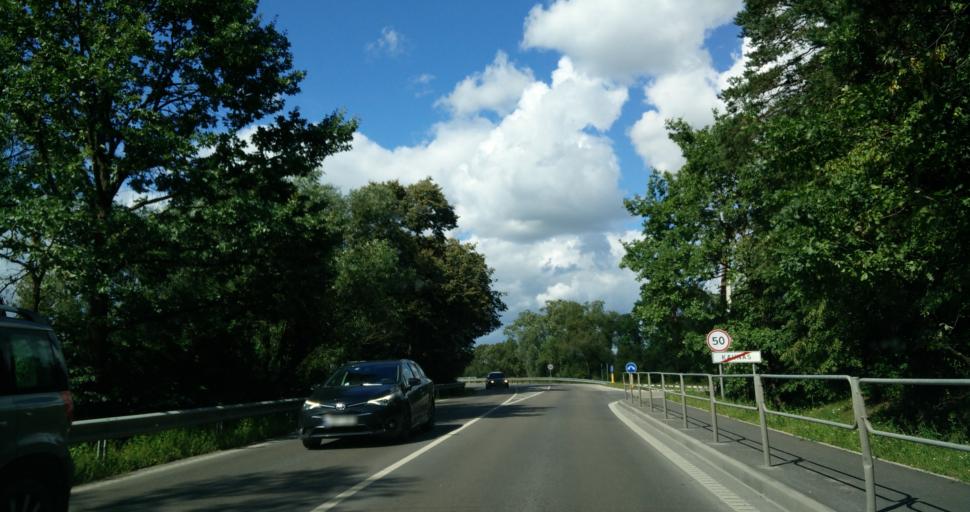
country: LT
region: Kauno apskritis
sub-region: Kauno rajonas
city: Akademija (Kaunas)
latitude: 54.9276
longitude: 23.7930
